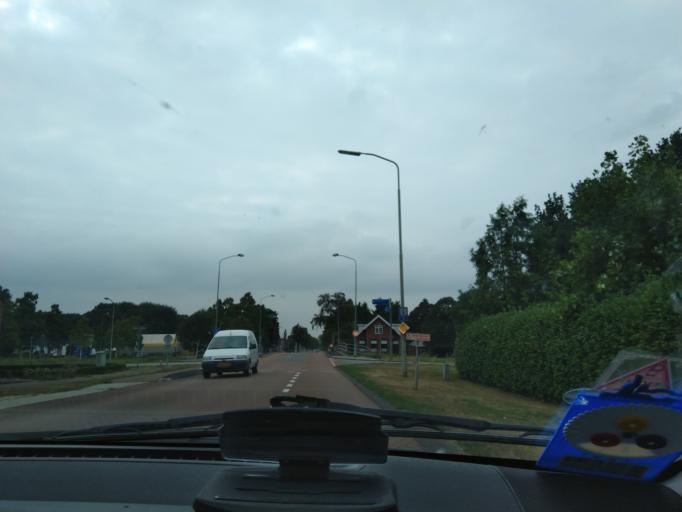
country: NL
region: Groningen
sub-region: Gemeente Vlagtwedde
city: Vlagtwedde
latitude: 53.0881
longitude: 7.1696
